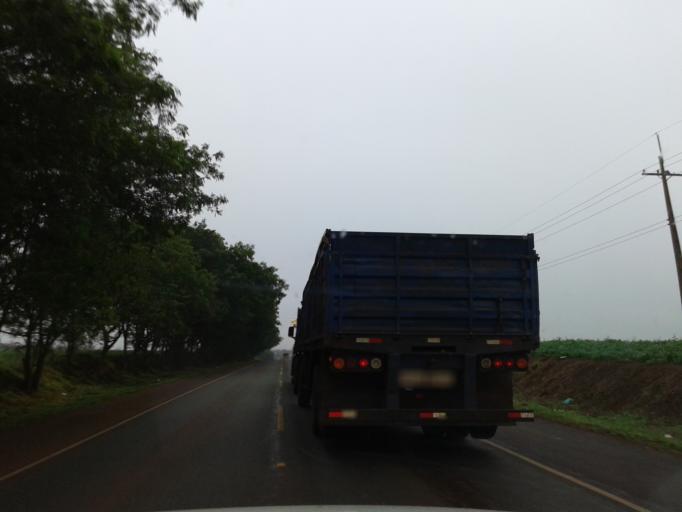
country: PY
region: Alto Parana
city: Naranjal
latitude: -25.9605
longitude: -55.1201
